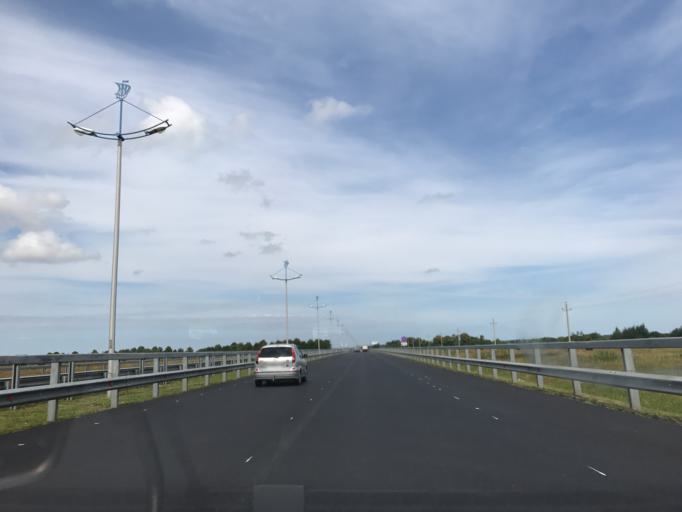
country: RU
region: Kaliningrad
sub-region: Zelenogradskiy Rayon
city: Zelenogradsk
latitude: 54.8763
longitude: 20.5370
